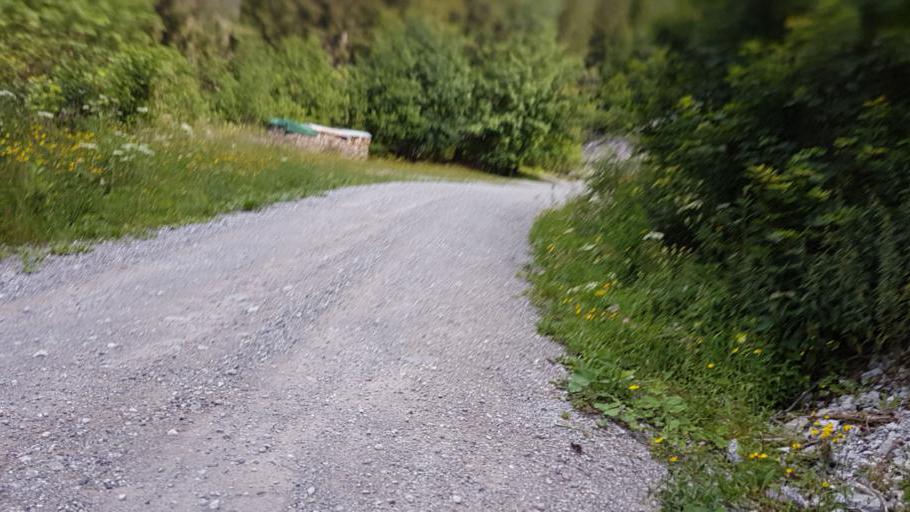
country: CH
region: Bern
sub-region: Obersimmental-Saanen District
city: Boltigen
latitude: 46.6825
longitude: 7.4503
